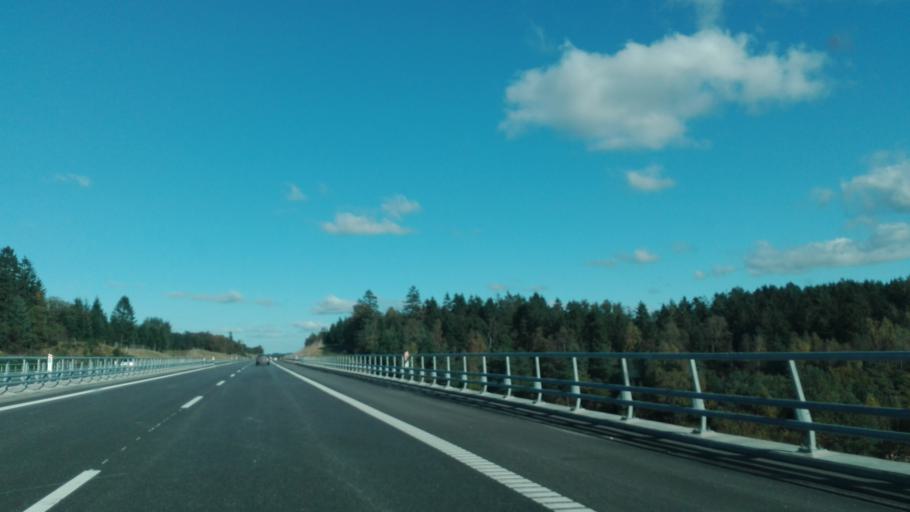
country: DK
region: Central Jutland
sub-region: Silkeborg Kommune
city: Silkeborg
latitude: 56.1699
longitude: 9.4732
